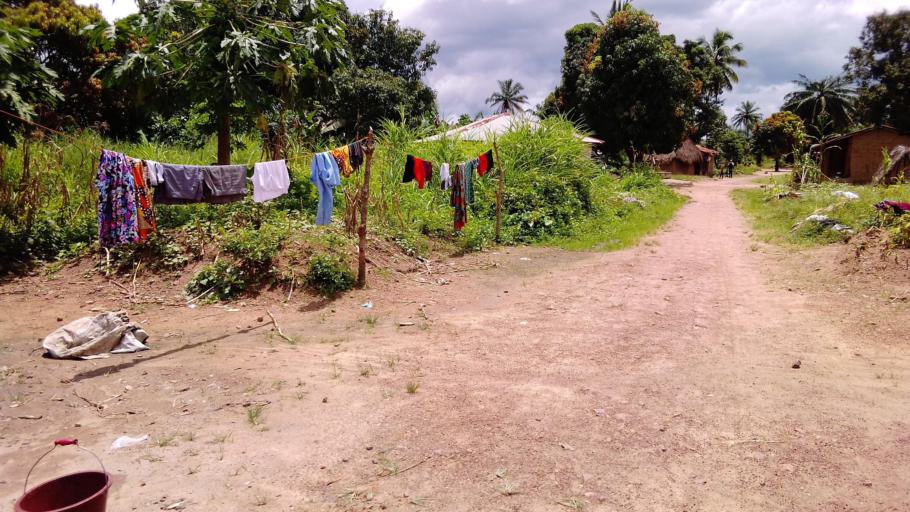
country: SL
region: Eastern Province
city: Koidu
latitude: 8.6691
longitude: -10.9538
